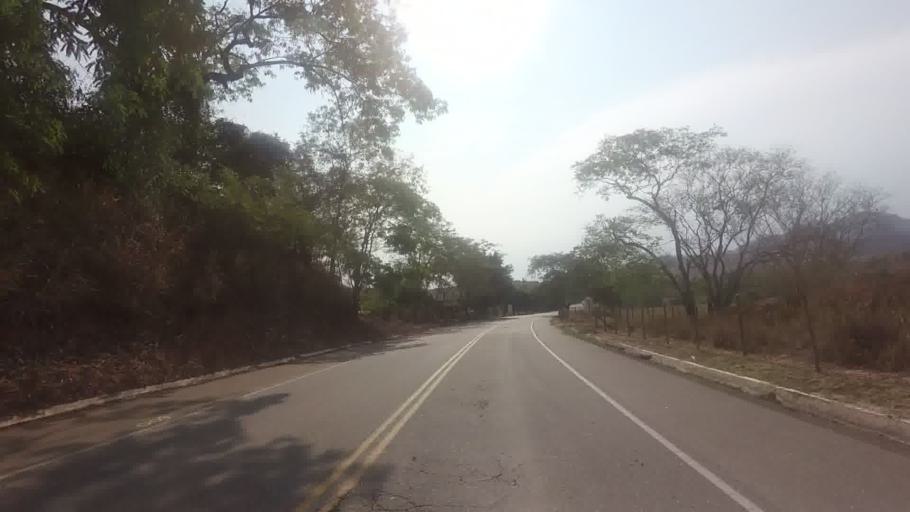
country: BR
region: Rio de Janeiro
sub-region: Bom Jesus Do Itabapoana
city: Bom Jesus do Itabapoana
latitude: -21.1372
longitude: -41.6392
